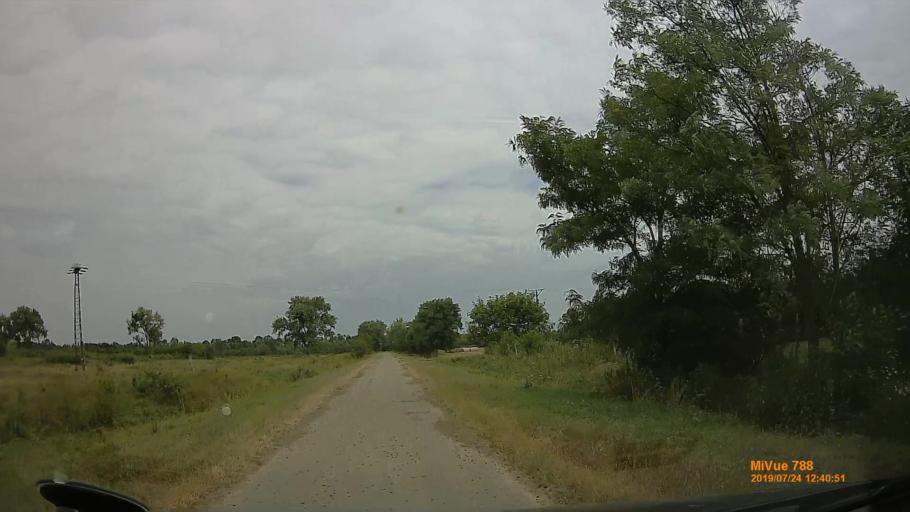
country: HU
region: Szabolcs-Szatmar-Bereg
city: Aranyosapati
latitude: 48.1930
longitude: 22.3166
